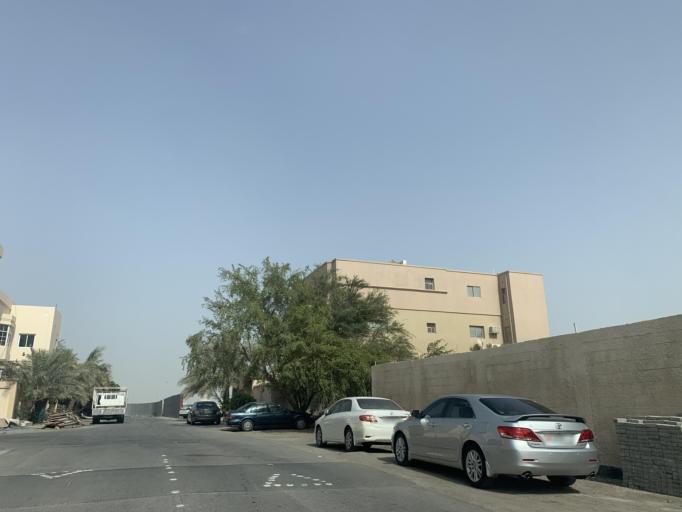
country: BH
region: Northern
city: Madinat `Isa
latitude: 26.1602
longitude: 50.5191
